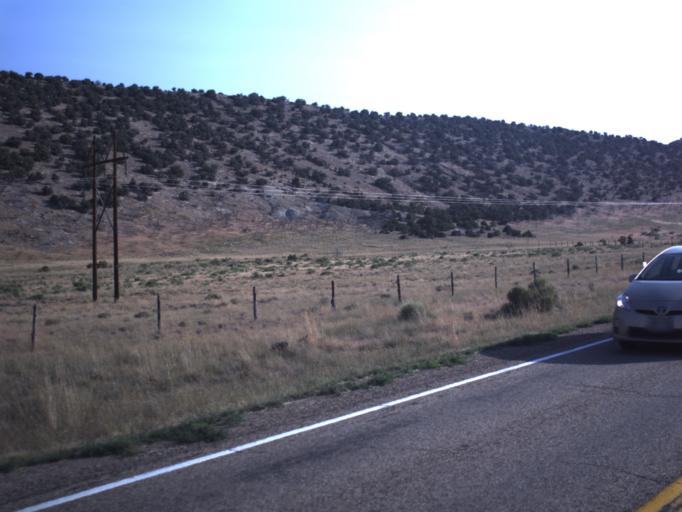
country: US
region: Utah
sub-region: Uintah County
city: Vernal
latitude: 40.5652
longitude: -109.5015
